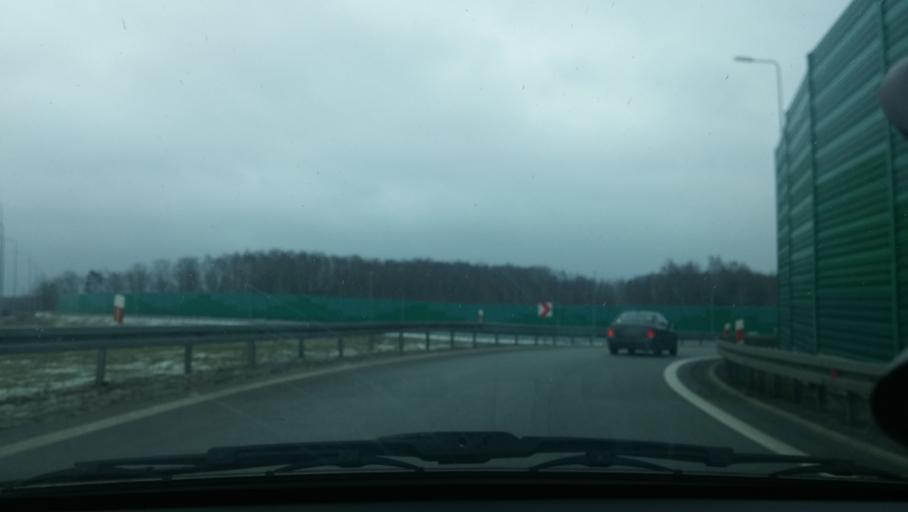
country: PL
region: Masovian Voivodeship
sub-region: Powiat minski
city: Kaluszyn
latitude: 52.1981
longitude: 21.7736
